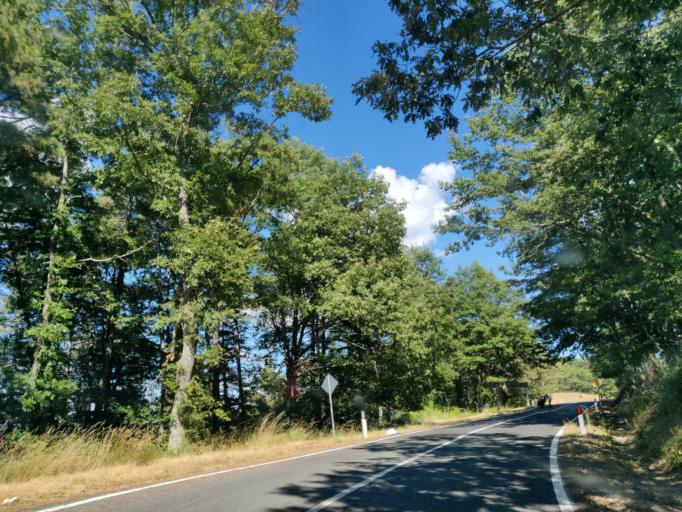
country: IT
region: Tuscany
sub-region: Provincia di Siena
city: Abbadia San Salvatore
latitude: 42.9100
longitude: 11.6808
